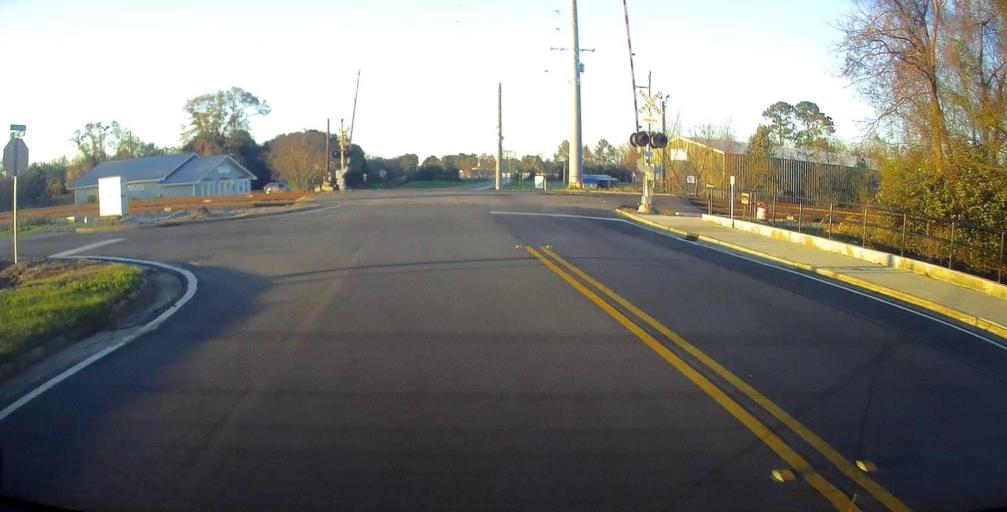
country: US
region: Georgia
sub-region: Crisp County
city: Cordele
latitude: 31.9661
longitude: -83.7653
